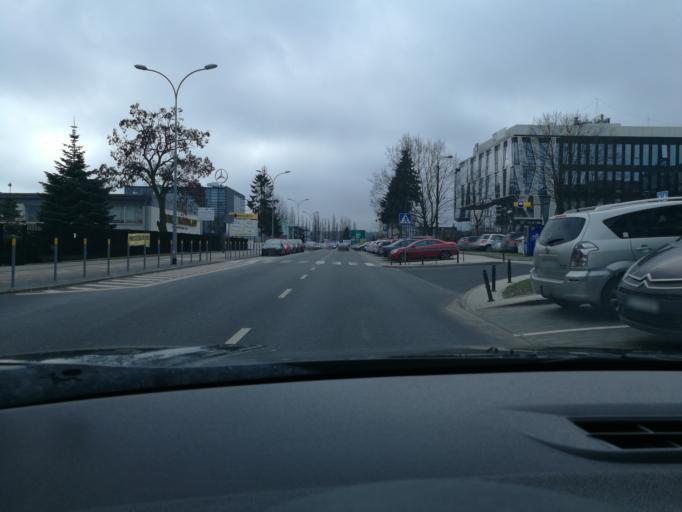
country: PL
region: Pomeranian Voivodeship
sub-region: Gdynia
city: Gdynia
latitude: 54.4941
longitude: 18.5348
